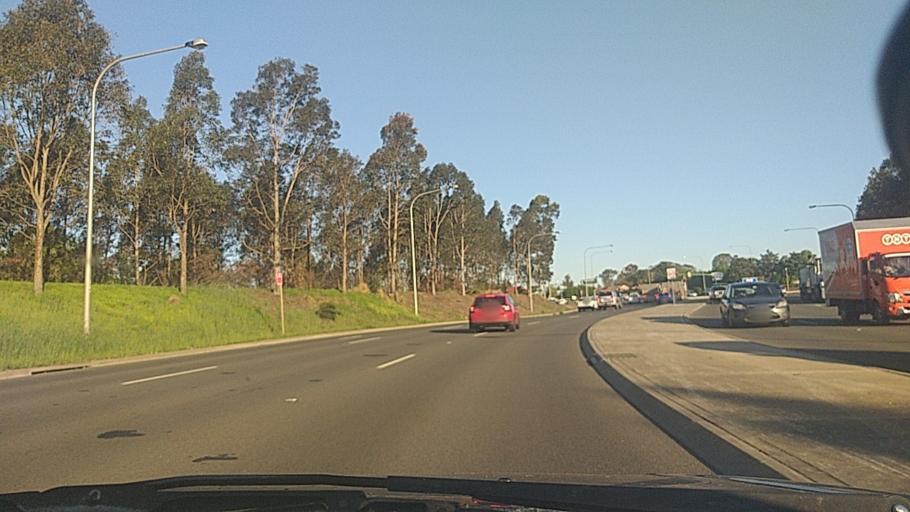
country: AU
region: New South Wales
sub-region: Camden
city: Narellan
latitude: -34.0383
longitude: 150.7384
